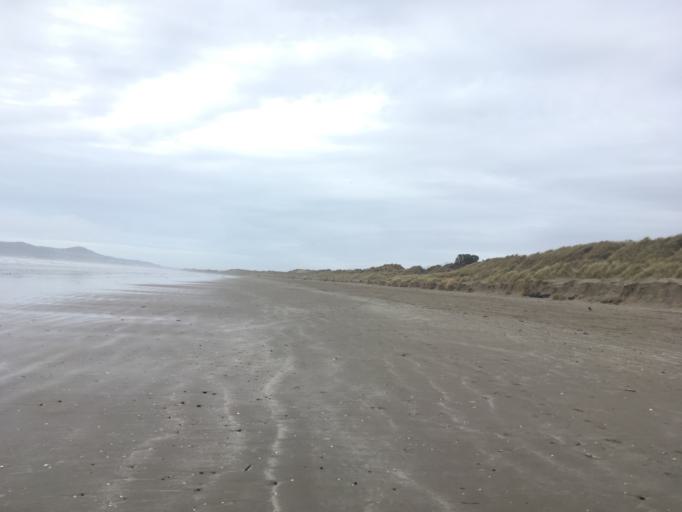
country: IE
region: Leinster
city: Portmarnock
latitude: 53.4255
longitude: -6.1234
